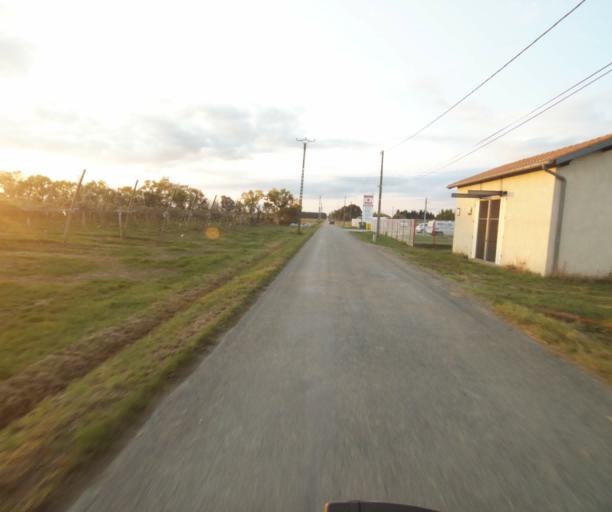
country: FR
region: Midi-Pyrenees
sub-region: Departement du Tarn-et-Garonne
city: Verdun-sur-Garonne
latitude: 43.8222
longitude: 1.2415
